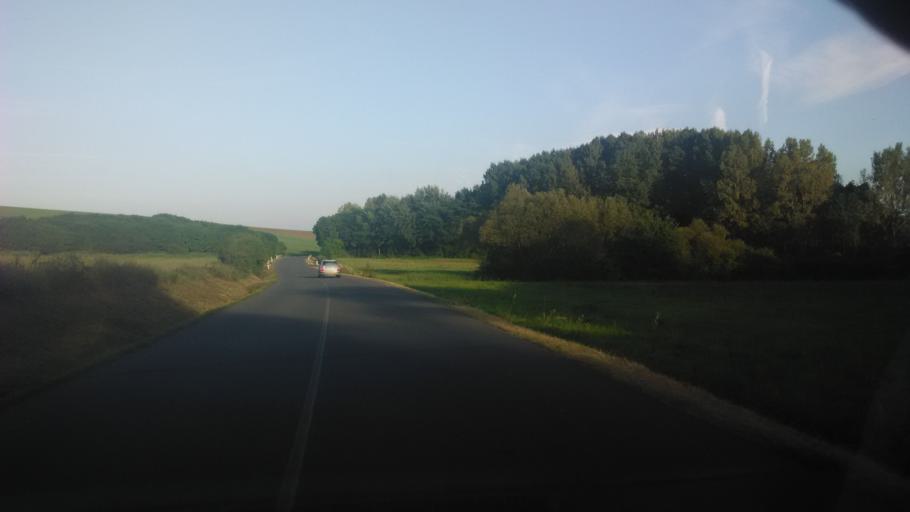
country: SK
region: Banskobystricky
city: Dudince
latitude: 48.1954
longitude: 18.8187
